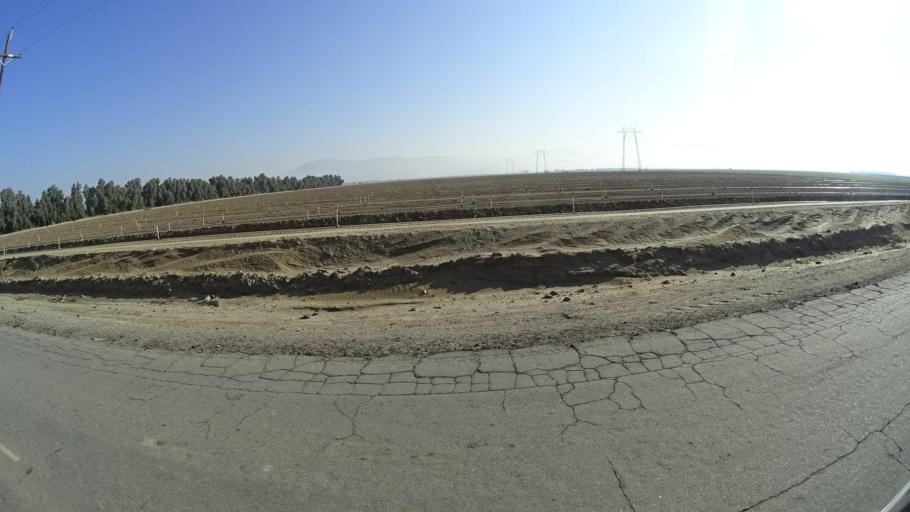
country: US
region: California
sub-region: Kern County
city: Weedpatch
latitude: 35.1273
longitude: -118.9681
